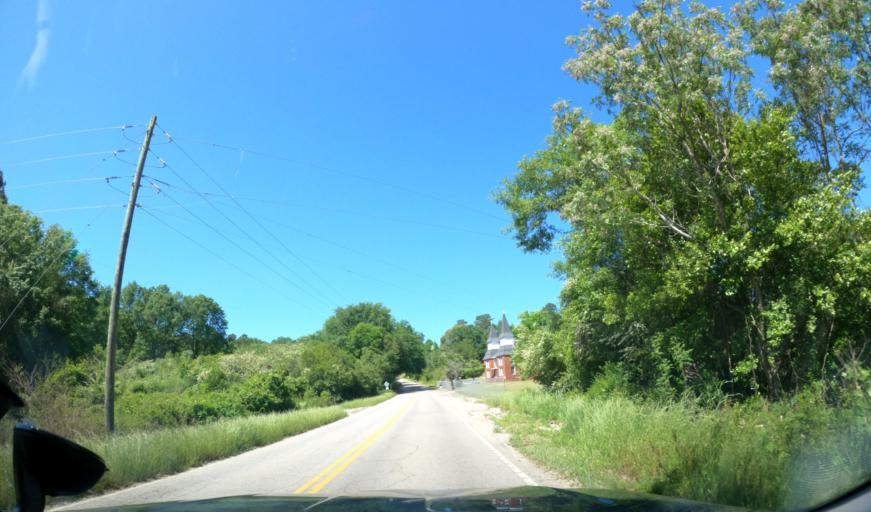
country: US
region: South Carolina
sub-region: Aiken County
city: Clearwater
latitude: 33.4896
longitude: -81.9064
